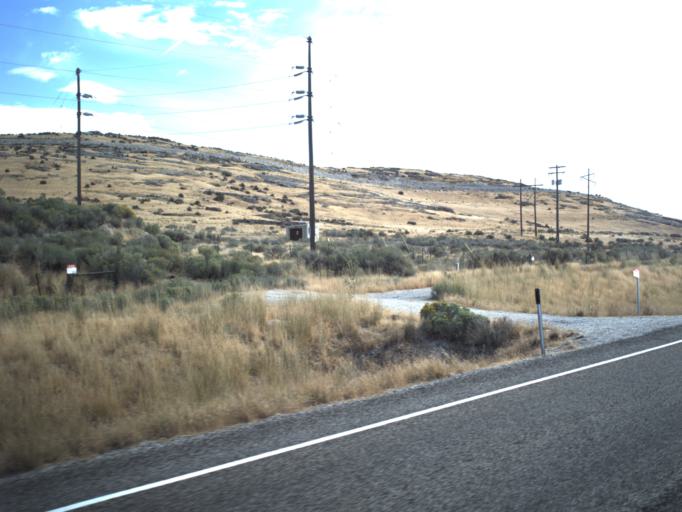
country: US
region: Utah
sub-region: Box Elder County
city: Tremonton
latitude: 41.6455
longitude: -112.4318
